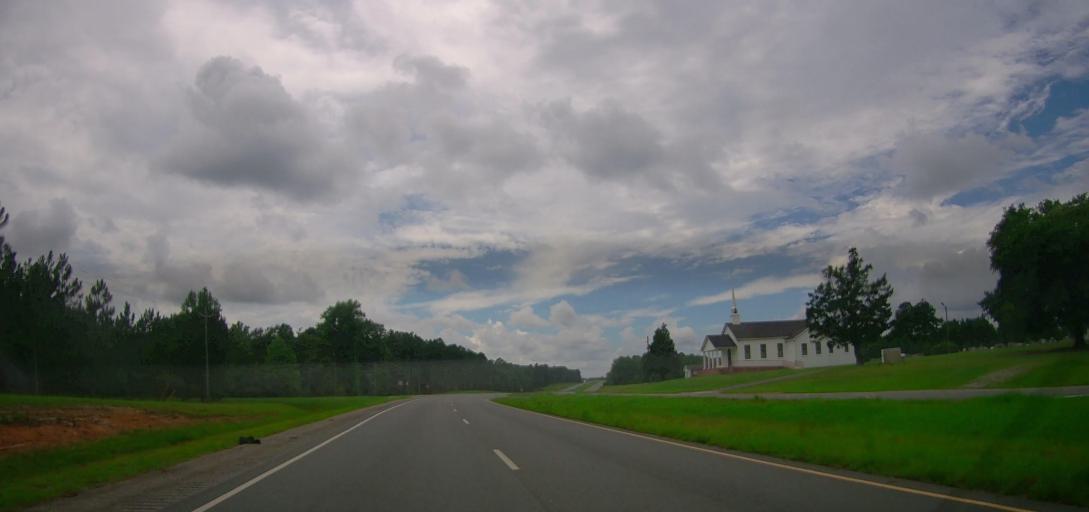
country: US
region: Georgia
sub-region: Telfair County
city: Helena
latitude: 32.1029
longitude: -83.0118
